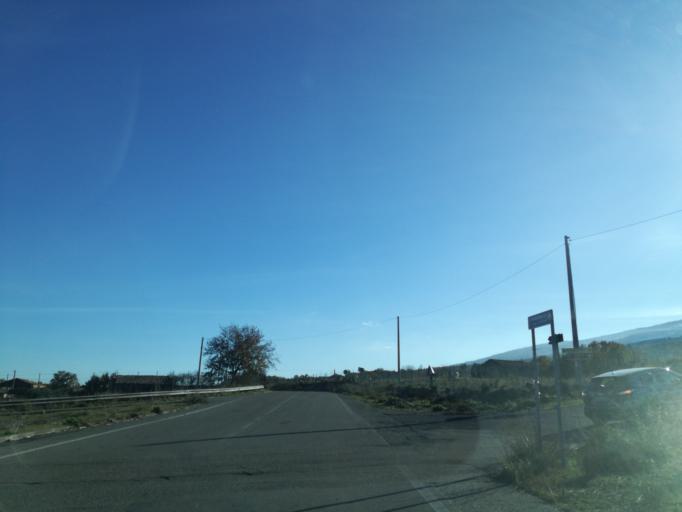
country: IT
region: Sicily
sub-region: Catania
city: Randazzo
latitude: 37.8666
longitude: 14.9796
